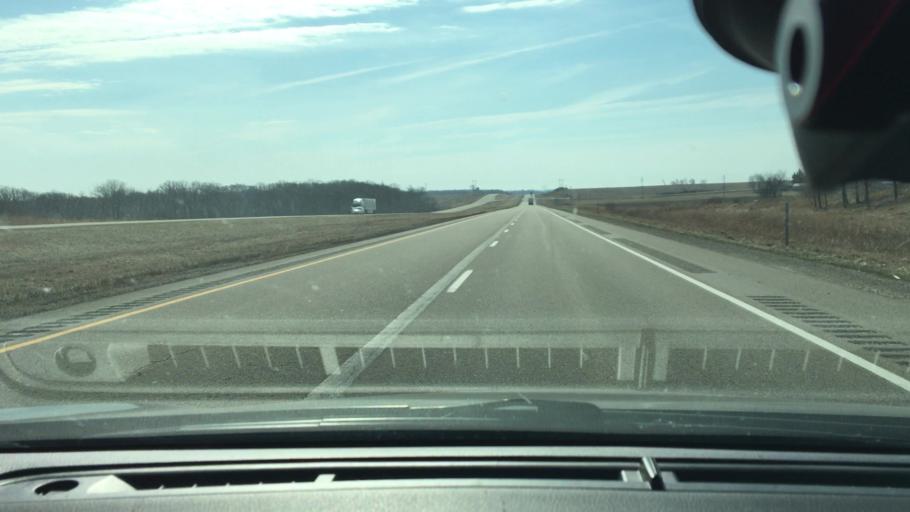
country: US
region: Iowa
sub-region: Floyd County
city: Charles City
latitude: 43.0062
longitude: -92.6204
